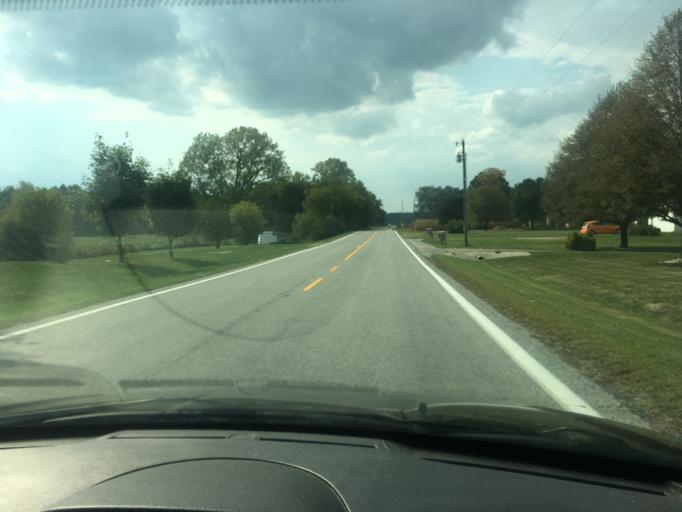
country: US
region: Ohio
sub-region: Champaign County
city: Urbana
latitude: 40.1567
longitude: -83.7712
